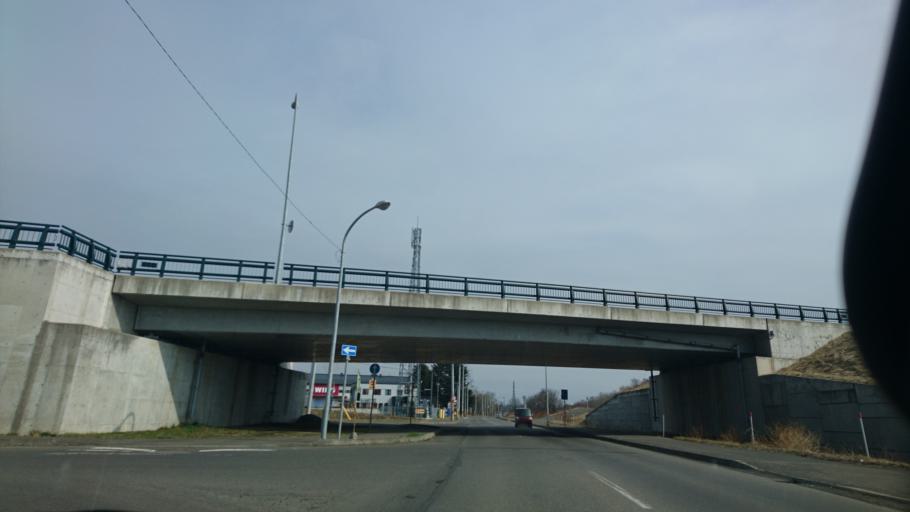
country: JP
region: Hokkaido
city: Otofuke
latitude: 42.9573
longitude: 143.2102
